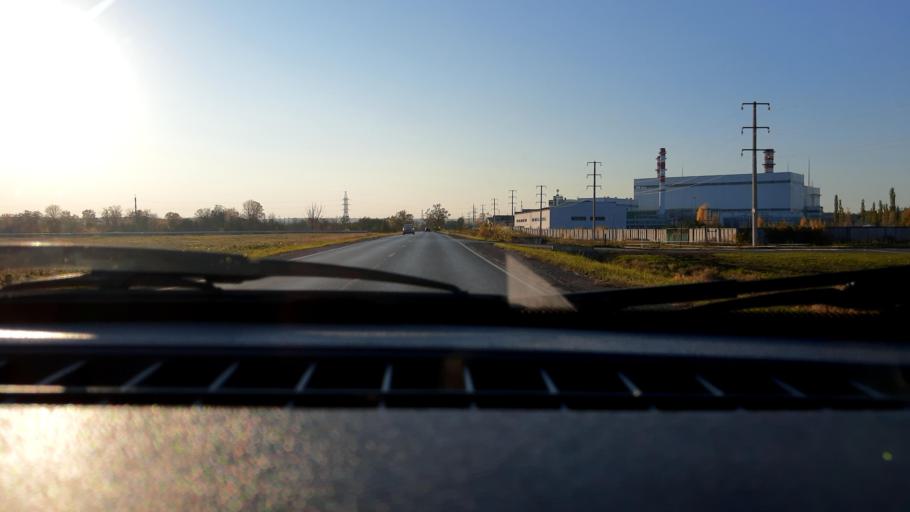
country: RU
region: Bashkortostan
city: Mikhaylovka
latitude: 54.7996
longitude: 55.8461
